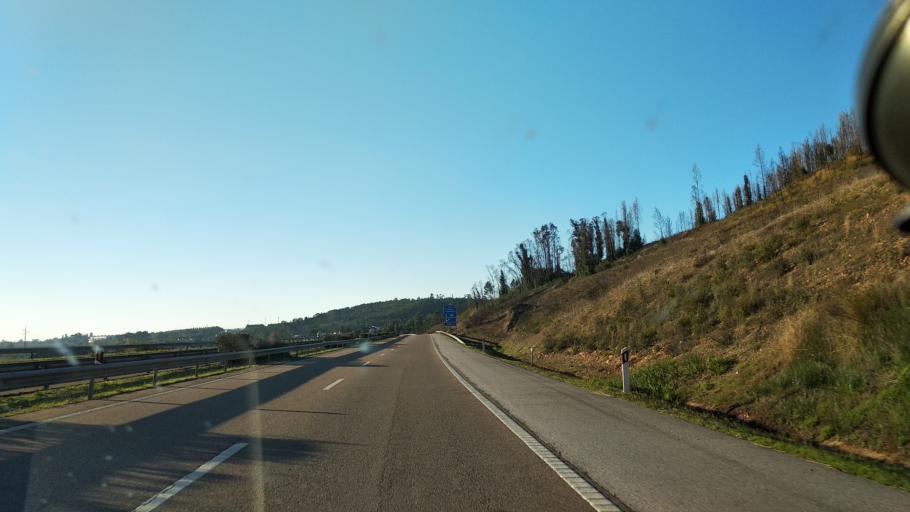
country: PT
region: Santarem
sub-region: Abrantes
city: Tramagal
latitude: 39.4857
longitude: -8.2579
